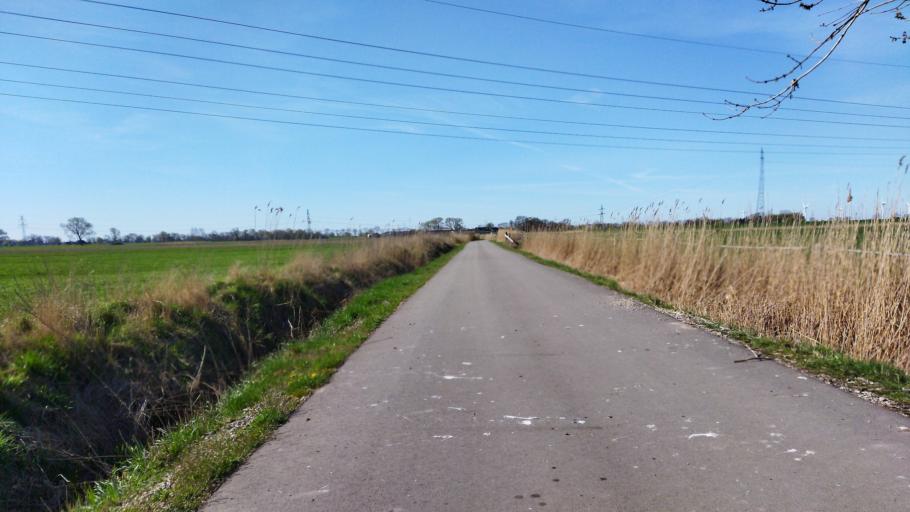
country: DE
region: Lower Saxony
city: Elsfleth
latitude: 53.2178
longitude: 8.4607
